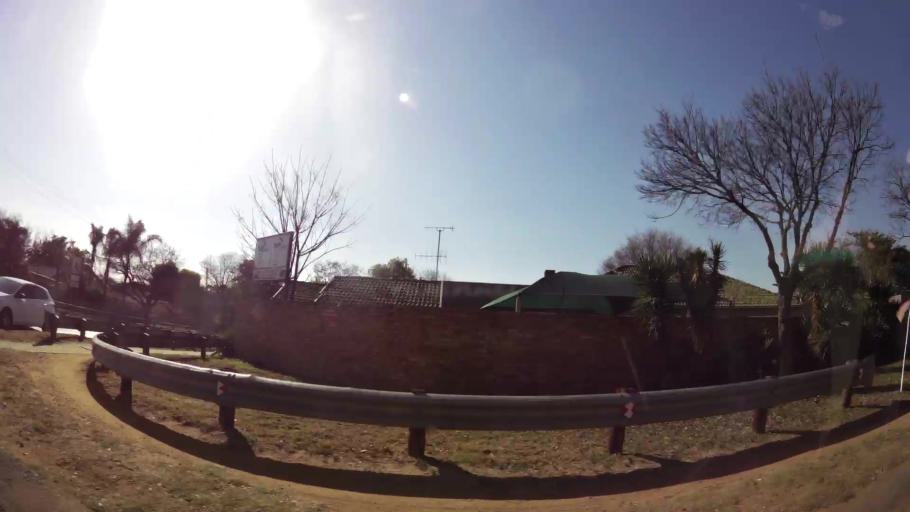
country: ZA
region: Gauteng
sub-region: City of Tshwane Metropolitan Municipality
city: Pretoria
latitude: -25.7233
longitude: 28.2425
